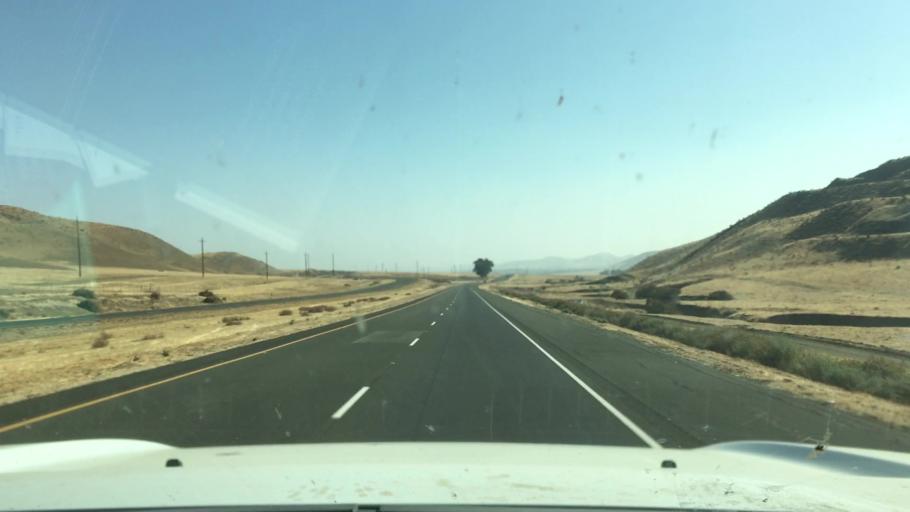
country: US
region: California
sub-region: San Luis Obispo County
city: Shandon
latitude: 35.7163
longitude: -120.1748
